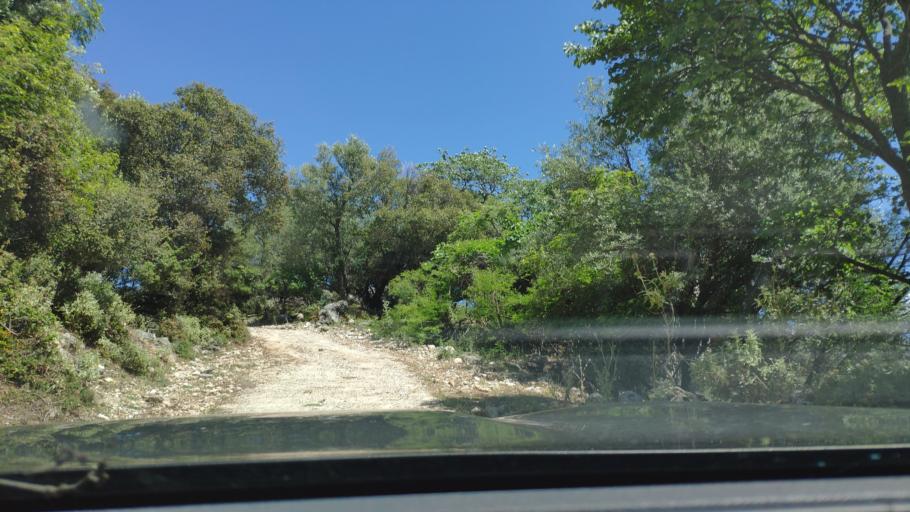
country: AL
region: Vlore
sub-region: Rrethi i Sarandes
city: Konispol
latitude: 39.6371
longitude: 20.1993
